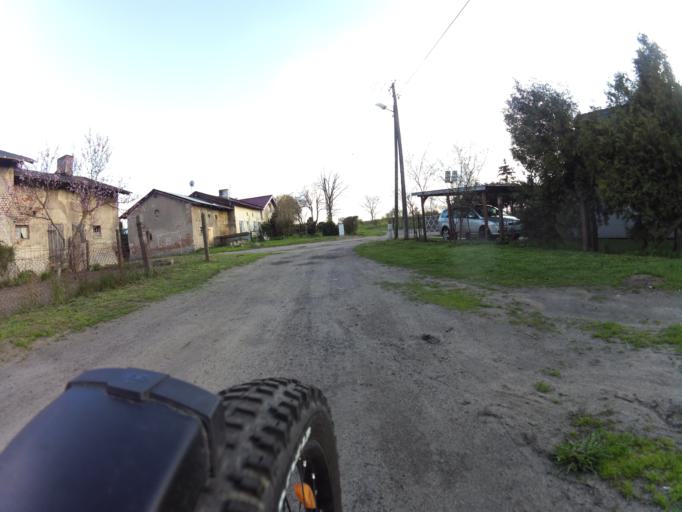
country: PL
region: West Pomeranian Voivodeship
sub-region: Powiat gryficki
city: Ploty
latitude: 53.7743
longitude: 15.2501
